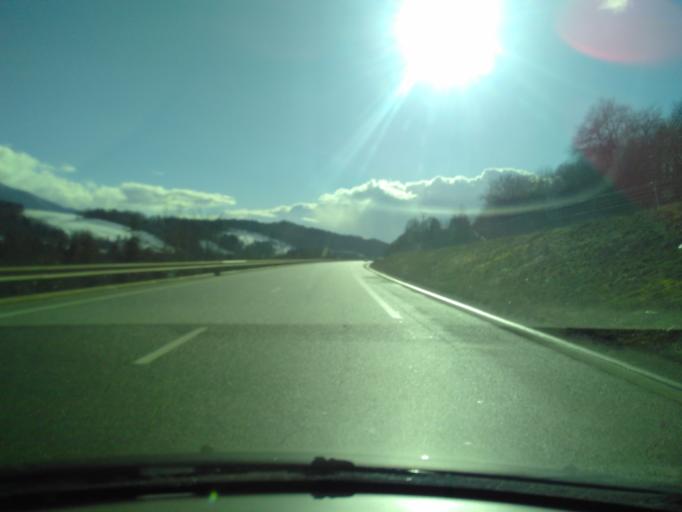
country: FR
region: Rhone-Alpes
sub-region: Departement de la Haute-Savoie
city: Evires
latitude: 46.0313
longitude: 6.2338
